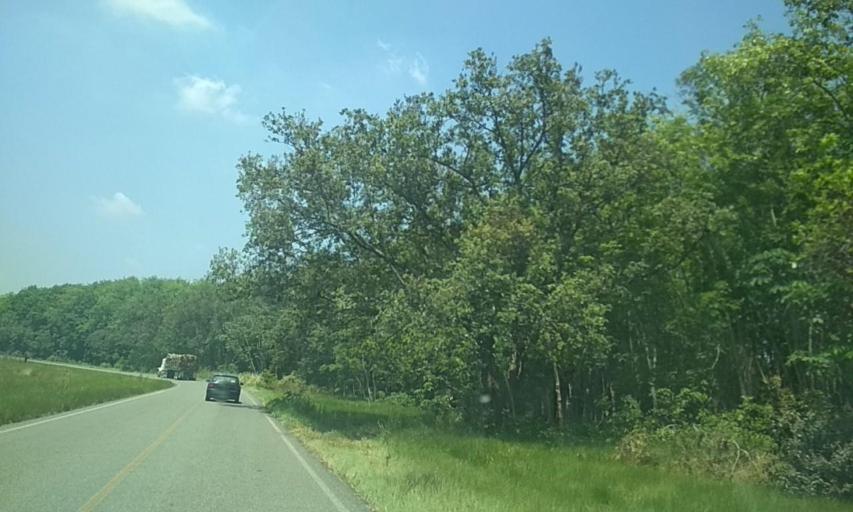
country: MX
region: Tabasco
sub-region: Huimanguillo
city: Paso de la Mina 3ra. Seccion
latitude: 17.8148
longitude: -93.6159
